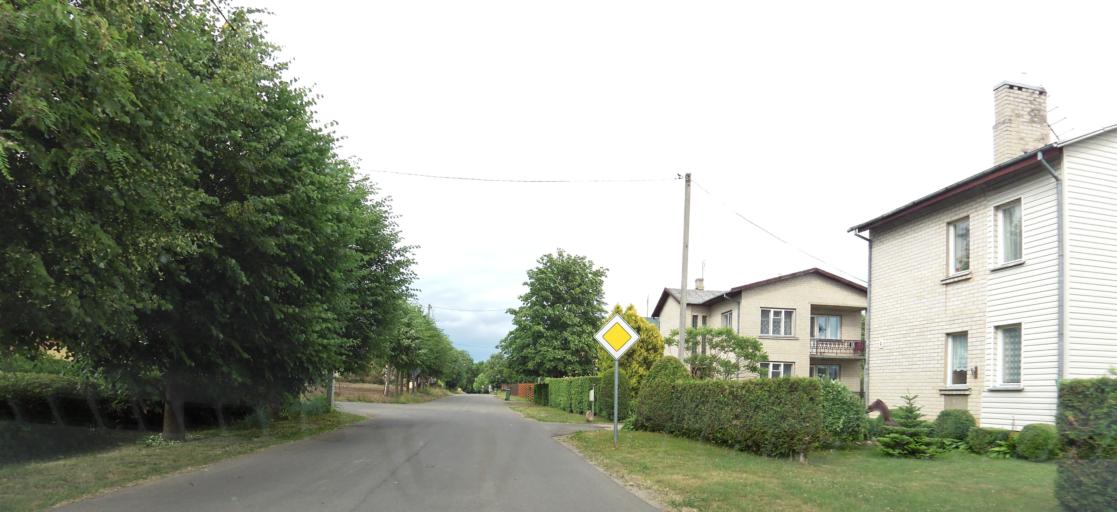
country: LT
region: Panevezys
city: Pasvalys
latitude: 56.0560
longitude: 24.3904
